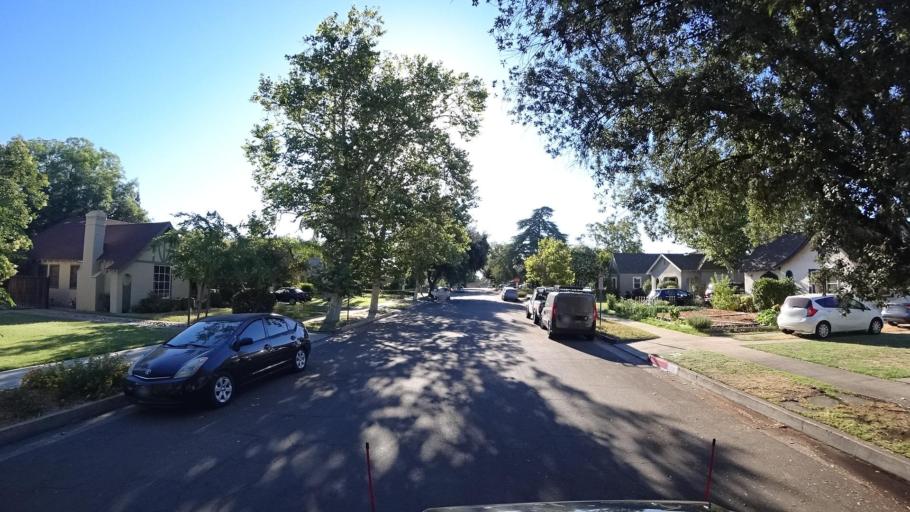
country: US
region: California
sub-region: Fresno County
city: Fresno
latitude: 36.7714
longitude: -119.7982
